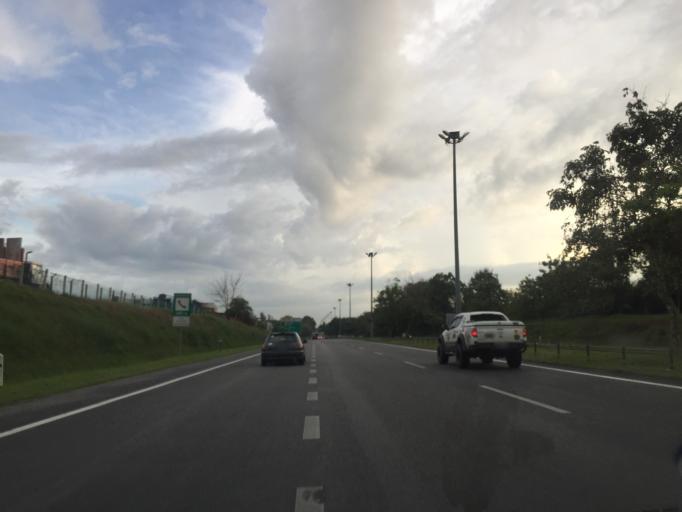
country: MY
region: Kedah
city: Gurun
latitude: 5.8255
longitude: 100.4893
